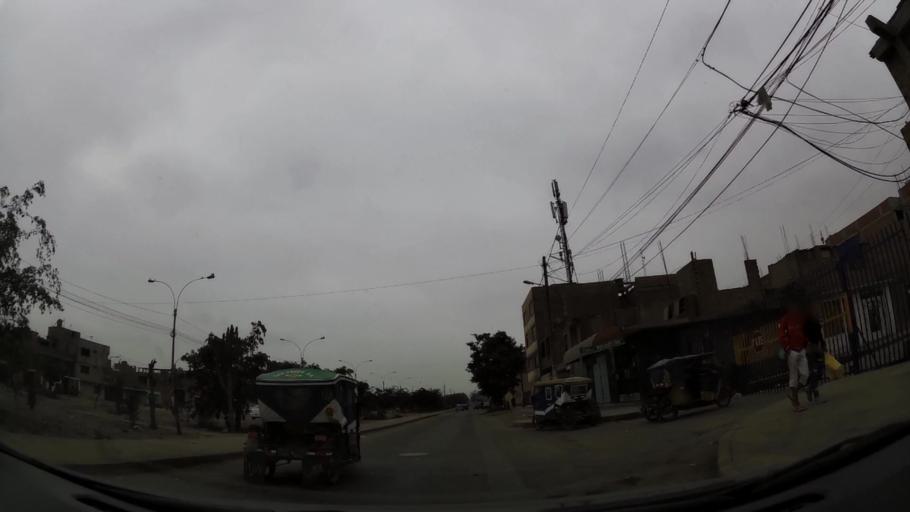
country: PE
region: Lima
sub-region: Lima
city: Independencia
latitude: -11.9704
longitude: -77.0605
